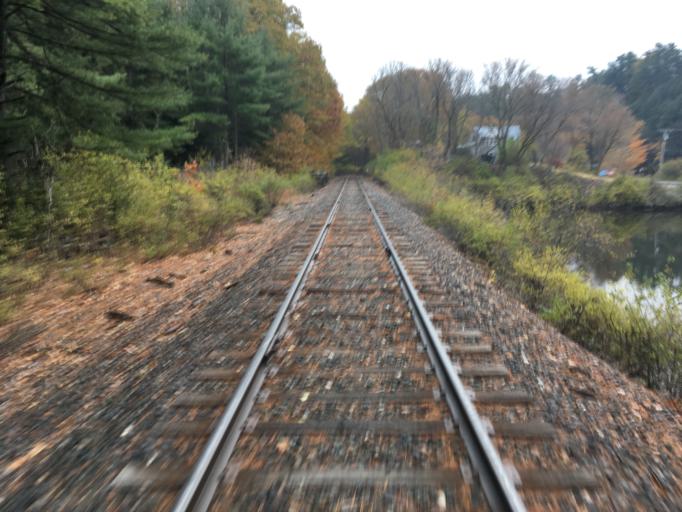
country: US
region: New Hampshire
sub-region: Grafton County
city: Hanover
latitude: 43.7086
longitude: -72.2978
